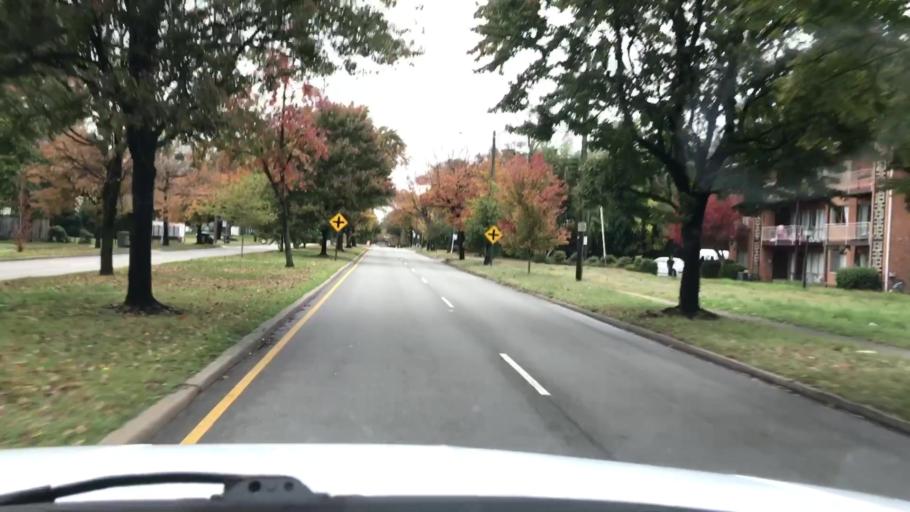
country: US
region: Virginia
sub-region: City of Richmond
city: Richmond
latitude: 37.5805
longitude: -77.4466
